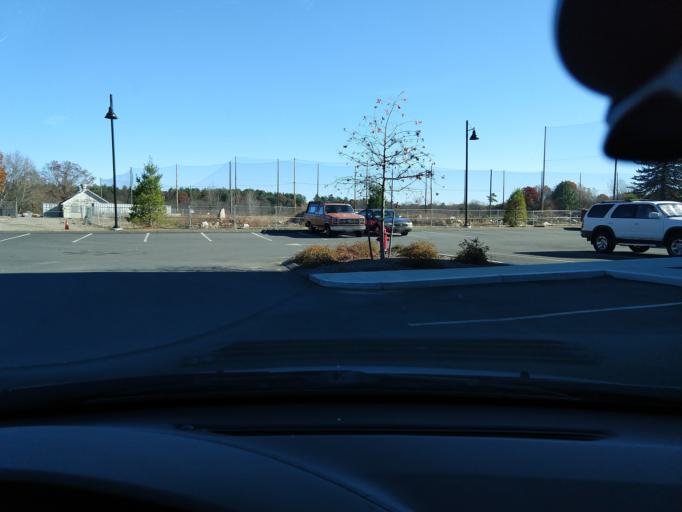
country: US
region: Massachusetts
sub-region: Middlesex County
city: Bedford
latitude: 42.5059
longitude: -71.2705
